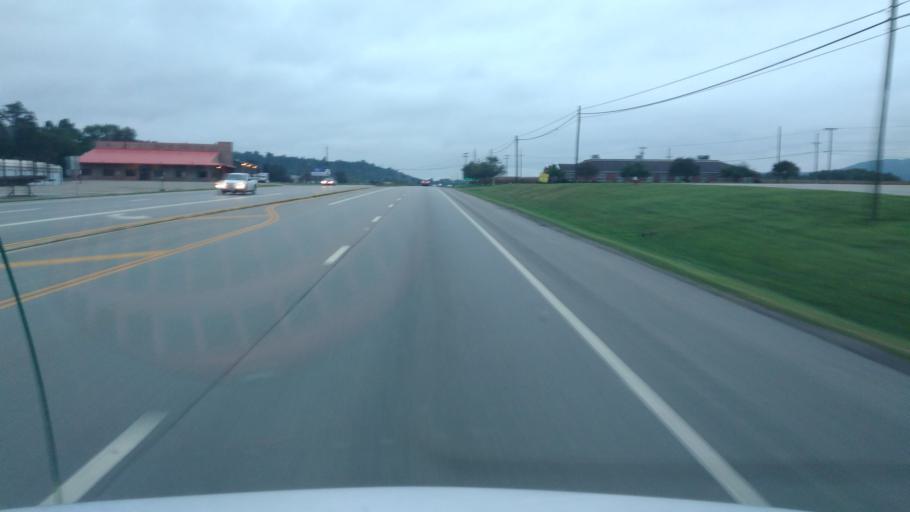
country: US
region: Ohio
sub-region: Pike County
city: Piketon
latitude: 39.0580
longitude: -83.0190
